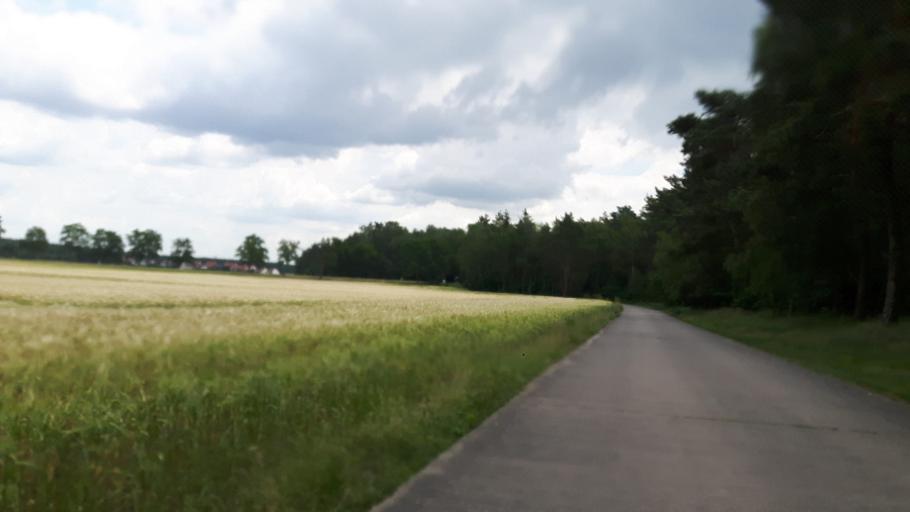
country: DE
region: Saxony-Anhalt
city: Schlaitz
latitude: 51.6517
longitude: 12.4335
